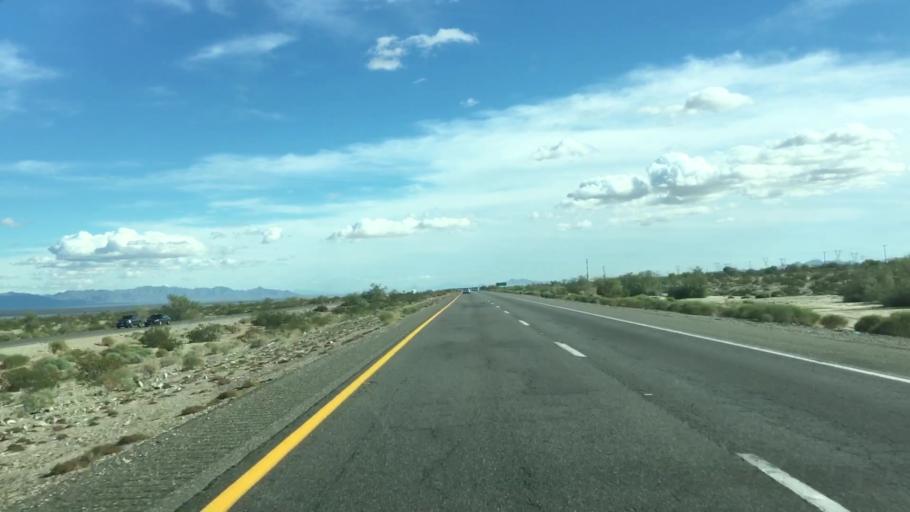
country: US
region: California
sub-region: Imperial County
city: Niland
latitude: 33.6888
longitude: -115.2653
